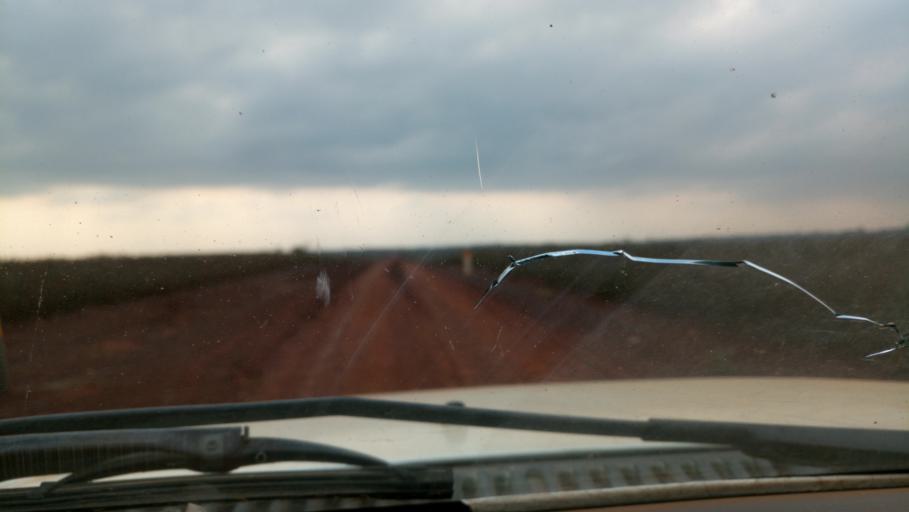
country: KE
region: Nairobi Area
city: Thika
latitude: -0.9809
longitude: 37.1135
